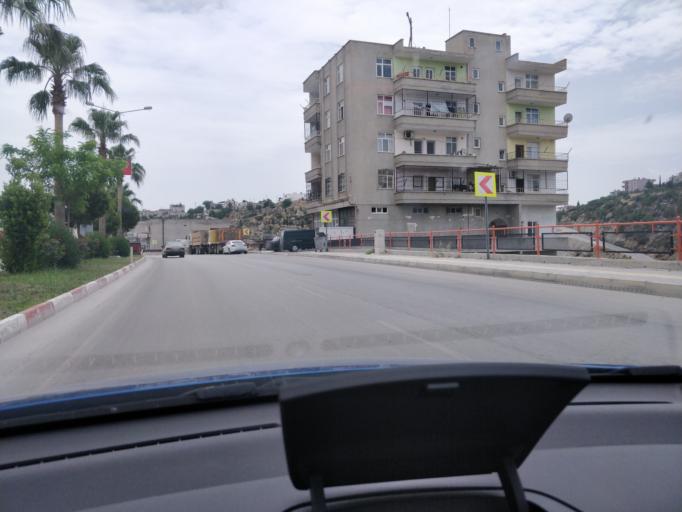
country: TR
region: Mersin
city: Mut
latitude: 36.6468
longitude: 33.4284
